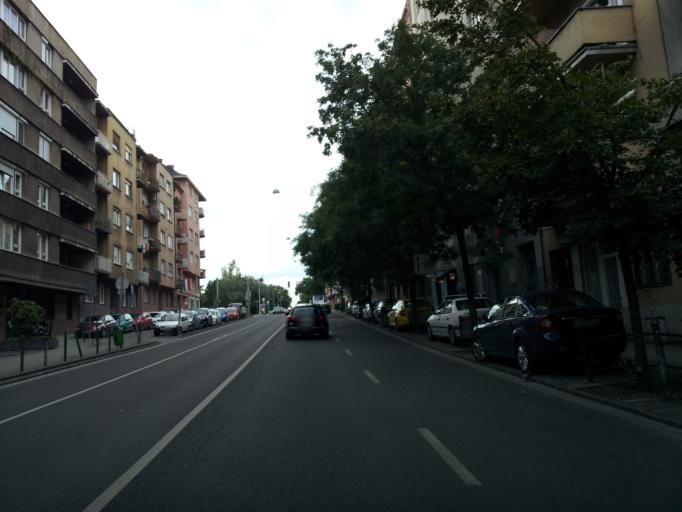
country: HU
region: Budapest
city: Budapest I. keruelet
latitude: 47.4984
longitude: 19.0321
